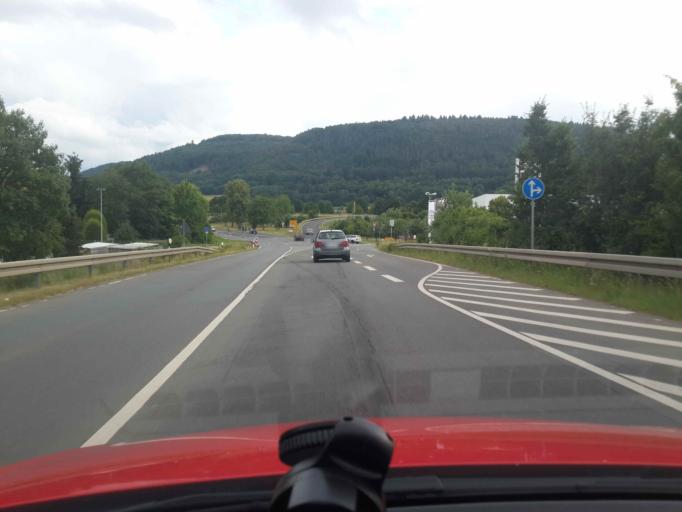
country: DE
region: Bavaria
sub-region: Regierungsbezirk Unterfranken
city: Kleinheubach
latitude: 49.7140
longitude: 9.2188
